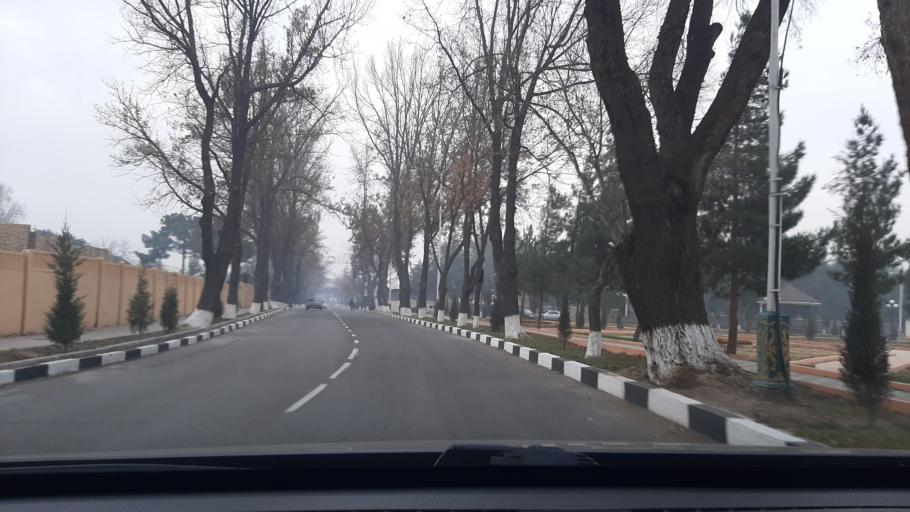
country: TJ
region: Viloyati Sughd
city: Chkalov
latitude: 40.2388
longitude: 69.6898
